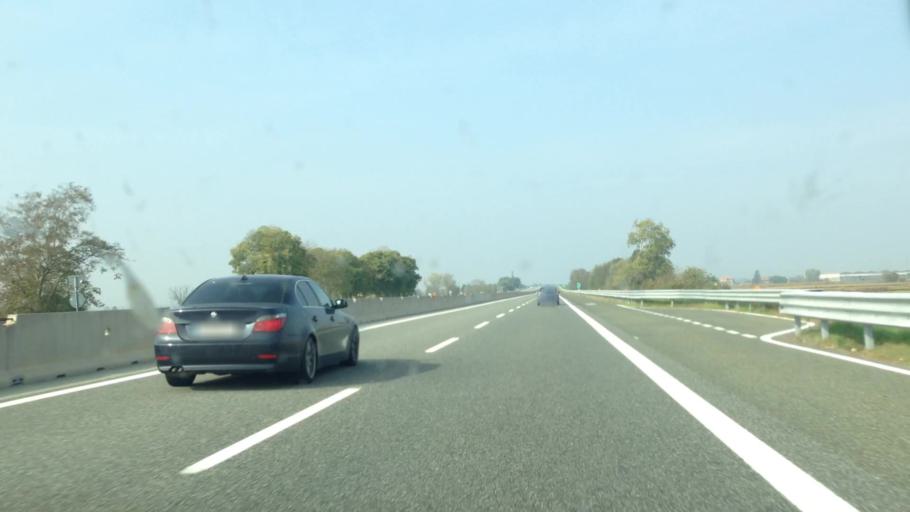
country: IT
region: Piedmont
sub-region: Provincia di Vercelli
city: Tronzano Vercellese
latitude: 45.3501
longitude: 8.1868
